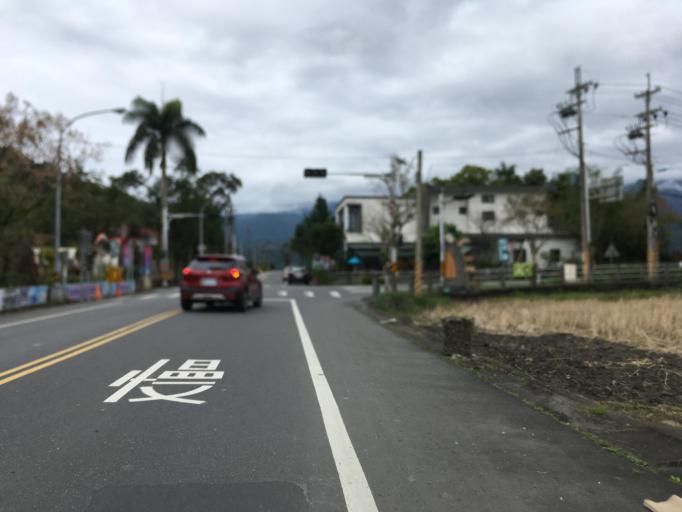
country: TW
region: Taiwan
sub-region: Yilan
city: Yilan
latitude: 24.6617
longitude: 121.6190
